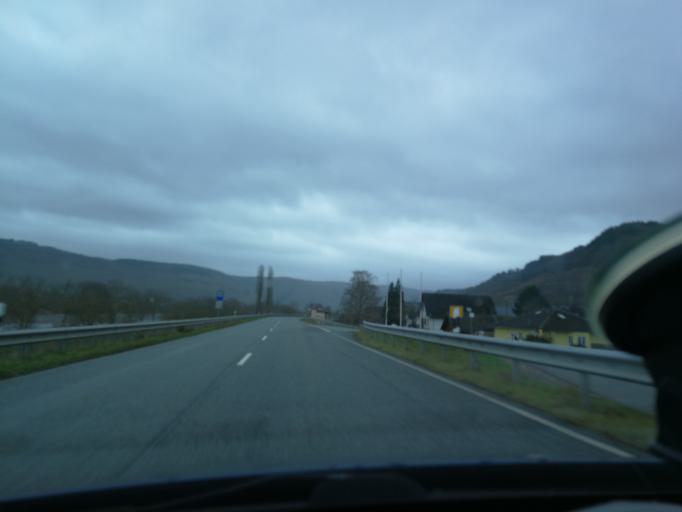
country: DE
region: Rheinland-Pfalz
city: Thornich
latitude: 49.8294
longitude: 6.8340
